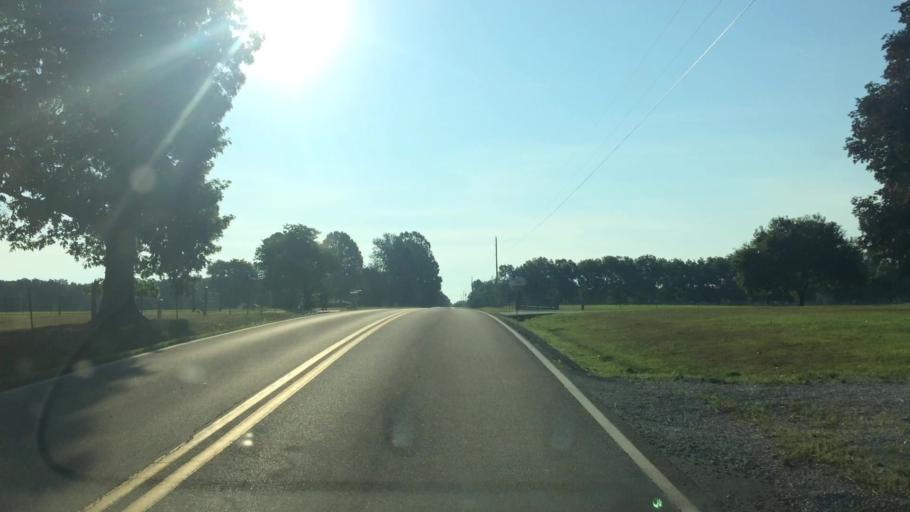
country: US
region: Missouri
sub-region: Greene County
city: Strafford
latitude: 37.2722
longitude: -93.2011
